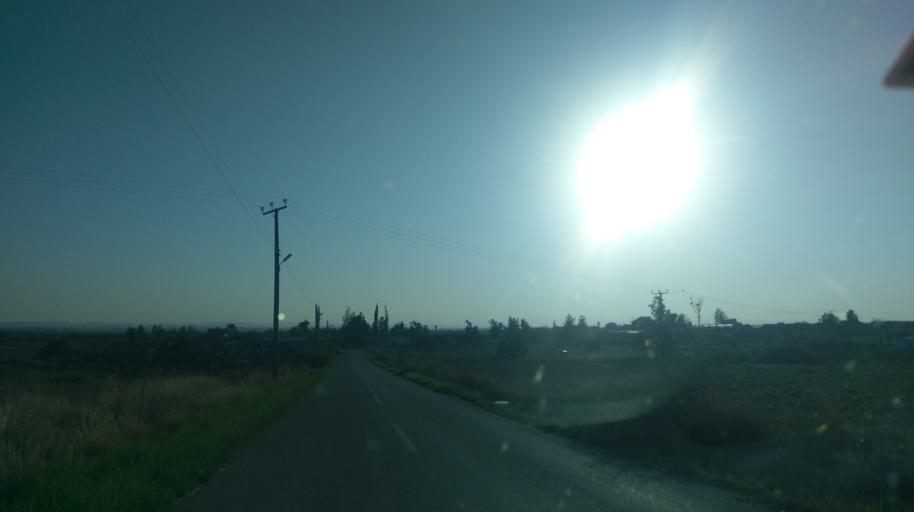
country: CY
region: Ammochostos
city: Lefkonoiko
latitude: 35.2487
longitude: 33.6501
